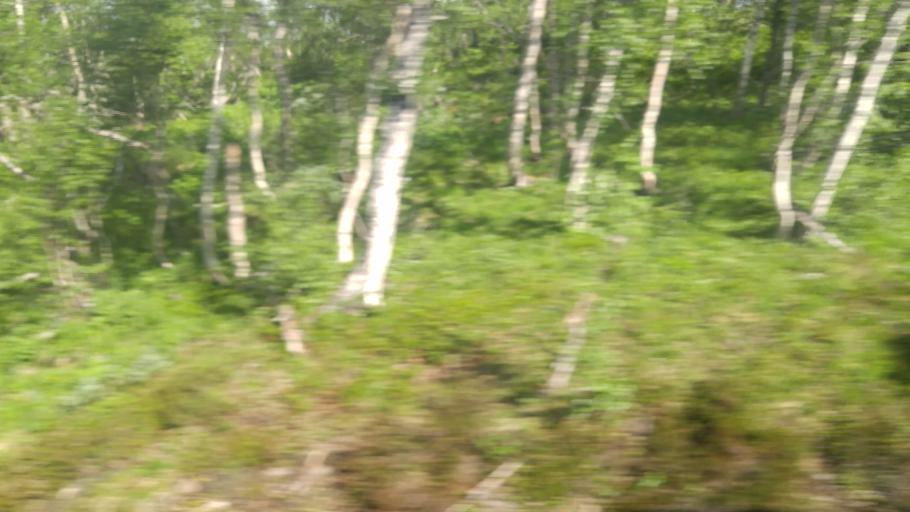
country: NO
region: Nord-Trondelag
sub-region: Meraker
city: Meraker
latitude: 63.3134
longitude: 12.1287
